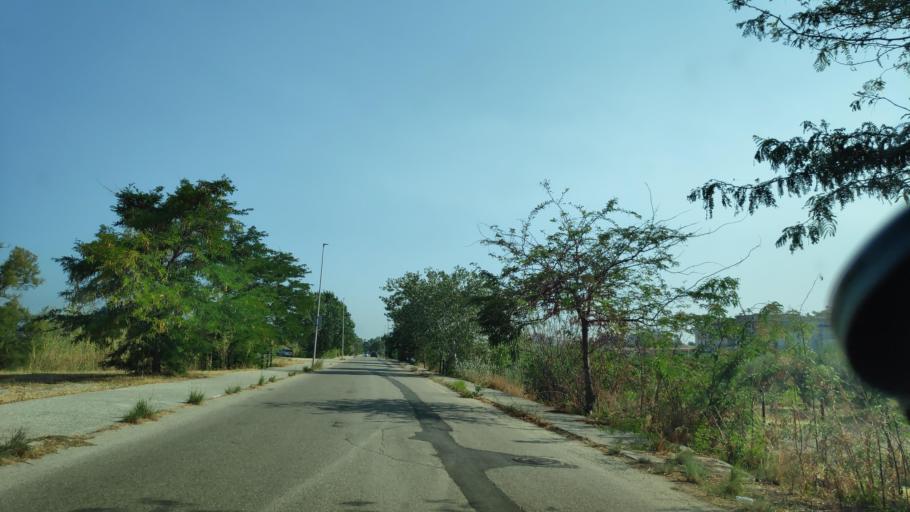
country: IT
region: Calabria
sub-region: Provincia di Catanzaro
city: Badolato Marina
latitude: 38.5777
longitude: 16.5680
